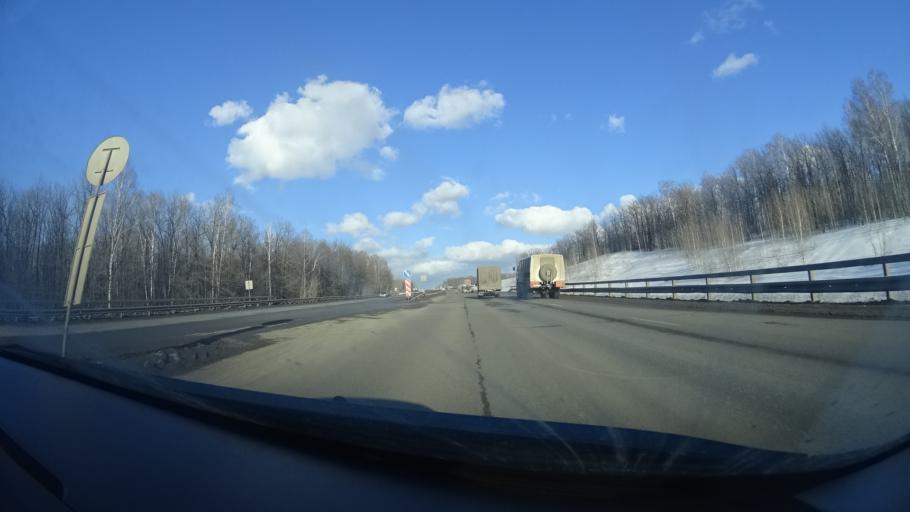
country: RU
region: Bashkortostan
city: Avdon
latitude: 54.6398
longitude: 55.6004
